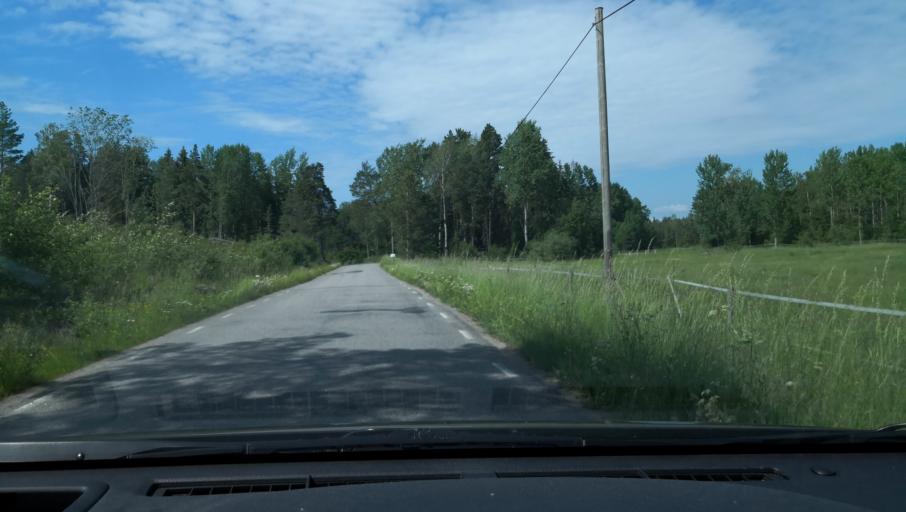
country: SE
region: Stockholm
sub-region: Sigtuna Kommun
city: Sigtuna
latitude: 59.6850
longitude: 17.6737
